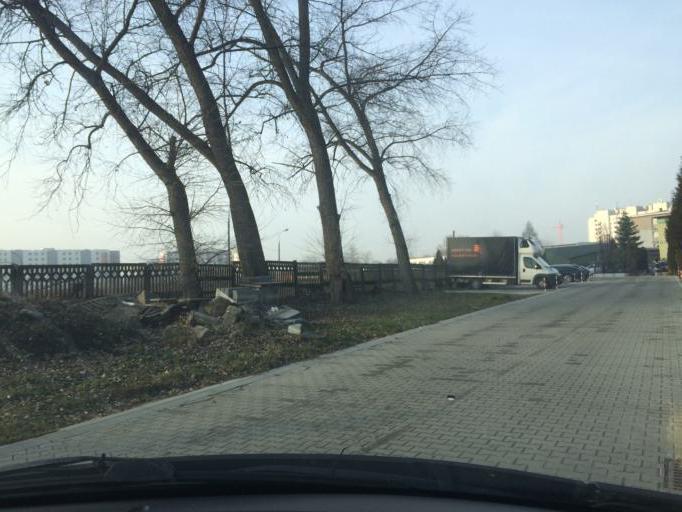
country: PL
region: Lesser Poland Voivodeship
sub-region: Krakow
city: Krakow
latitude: 50.0619
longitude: 20.0145
